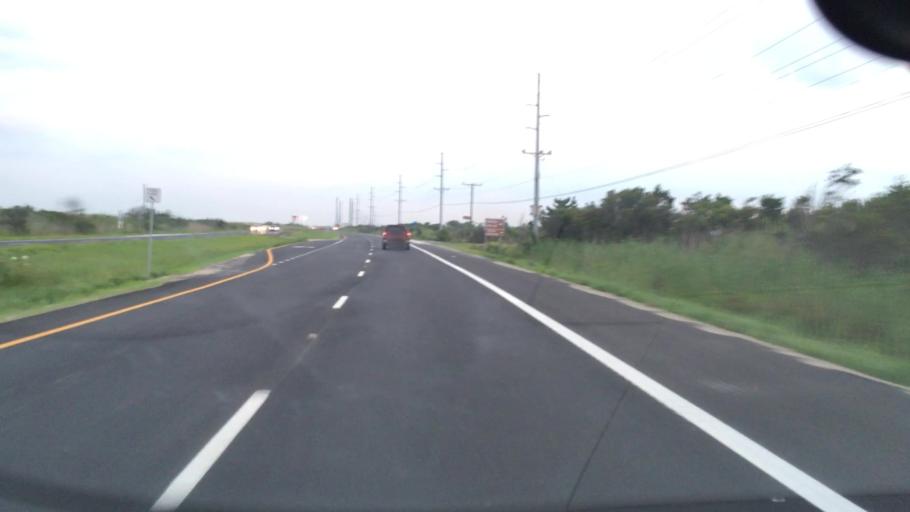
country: US
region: Delaware
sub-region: Sussex County
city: Long Neck
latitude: 38.6288
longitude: -75.0678
